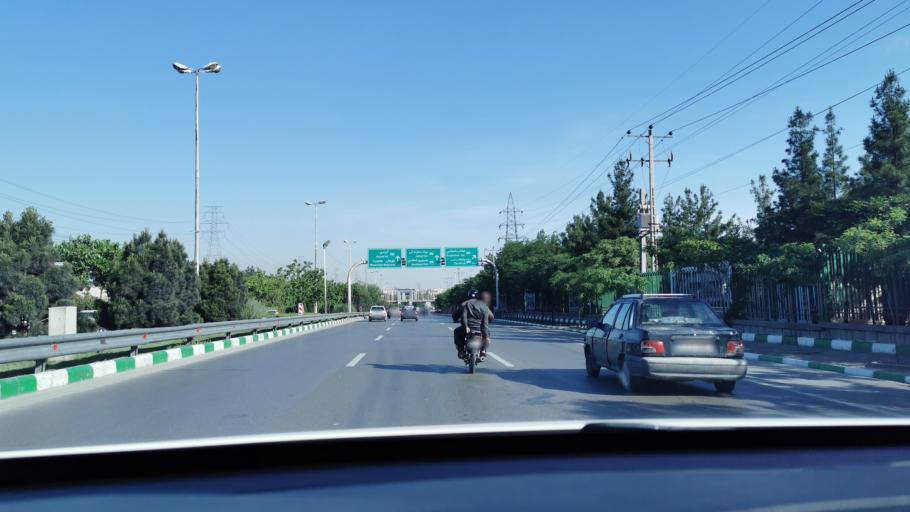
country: IR
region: Razavi Khorasan
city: Mashhad
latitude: 36.2592
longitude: 59.5874
